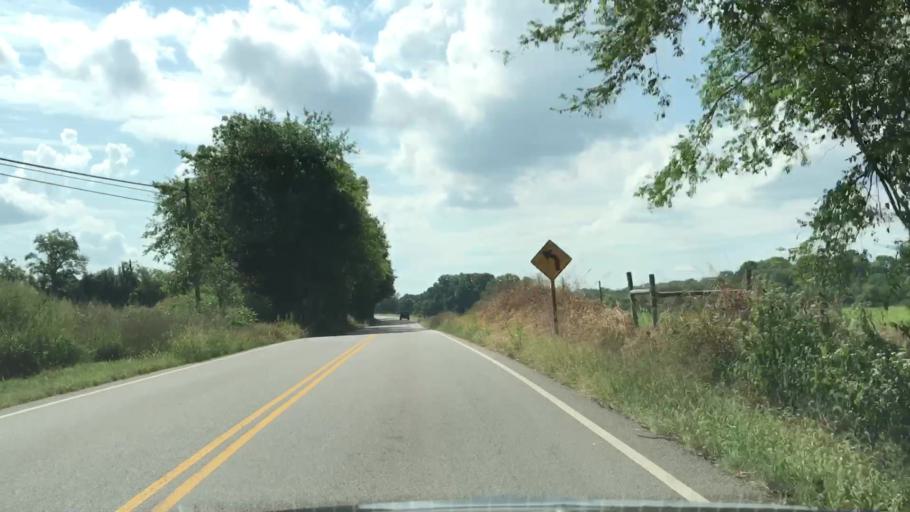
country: US
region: Tennessee
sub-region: Trousdale County
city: Hartsville
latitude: 36.4152
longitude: -86.1799
